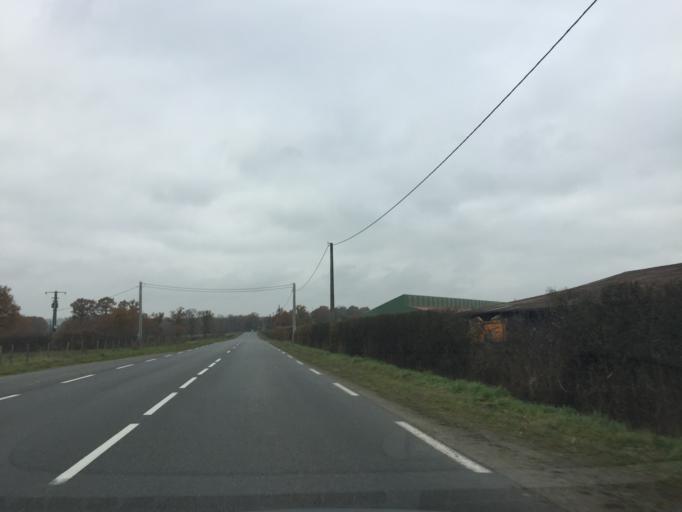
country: FR
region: Limousin
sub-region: Departement de la Creuse
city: Gouzon
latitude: 46.1677
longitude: 2.2182
